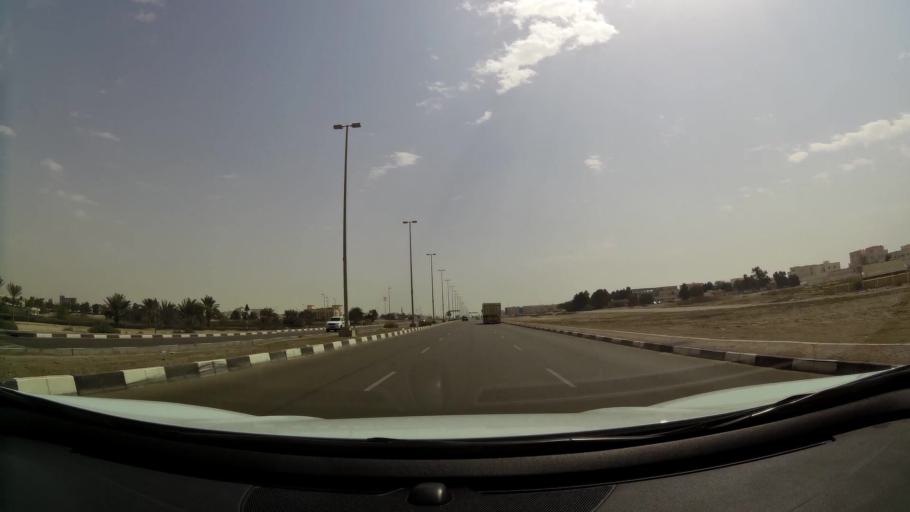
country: AE
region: Abu Dhabi
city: Abu Dhabi
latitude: 24.3040
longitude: 54.6303
